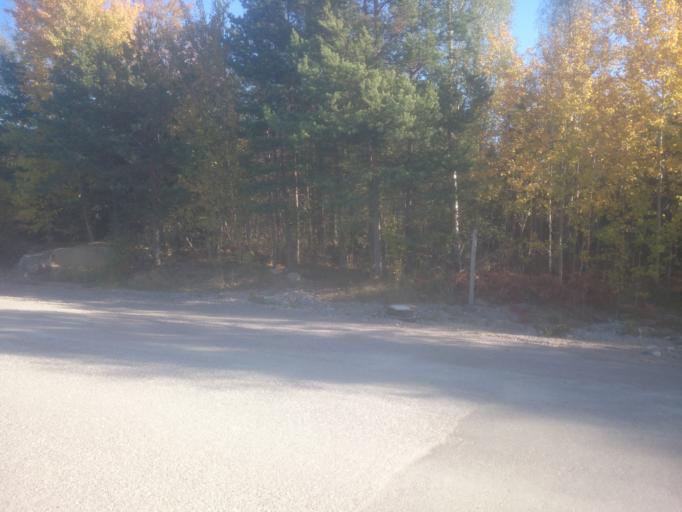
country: SE
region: Stockholm
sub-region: Upplands-Bro Kommun
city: Kungsaengen
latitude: 59.4933
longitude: 17.7366
